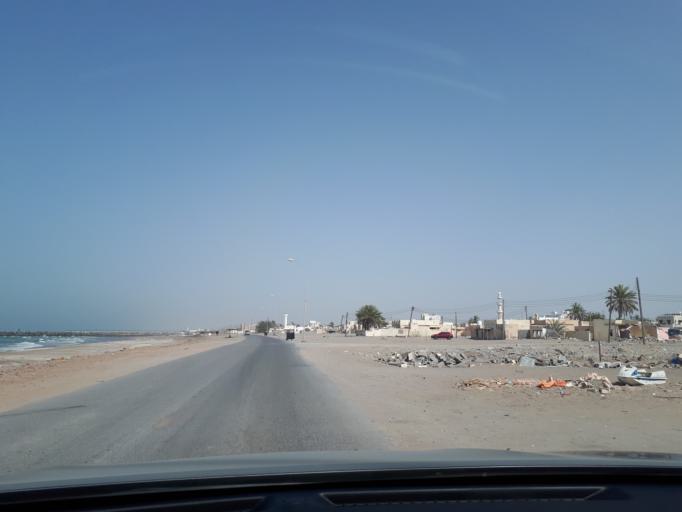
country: OM
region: Al Batinah
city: Barka'
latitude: 23.7111
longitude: 57.8846
